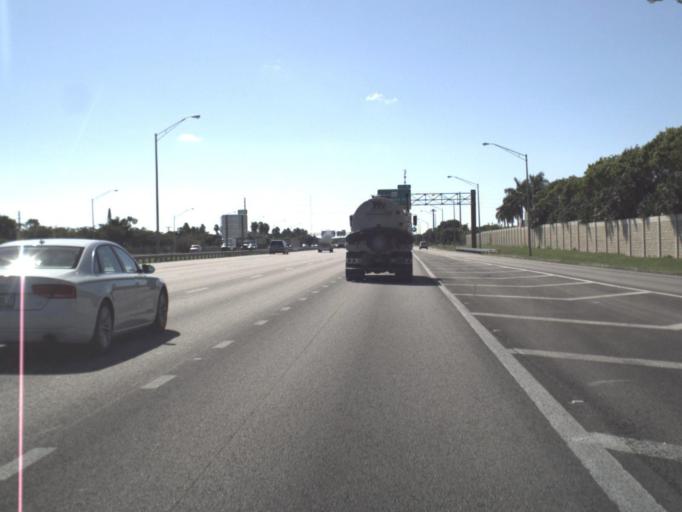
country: US
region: Florida
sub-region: Miami-Dade County
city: Three Lakes
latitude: 25.6427
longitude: -80.3858
